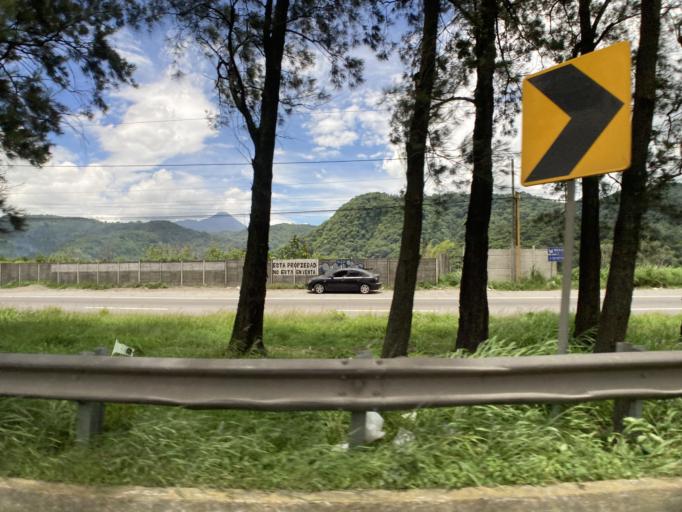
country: GT
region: Escuintla
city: Palin
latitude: 14.4137
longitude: -90.6750
